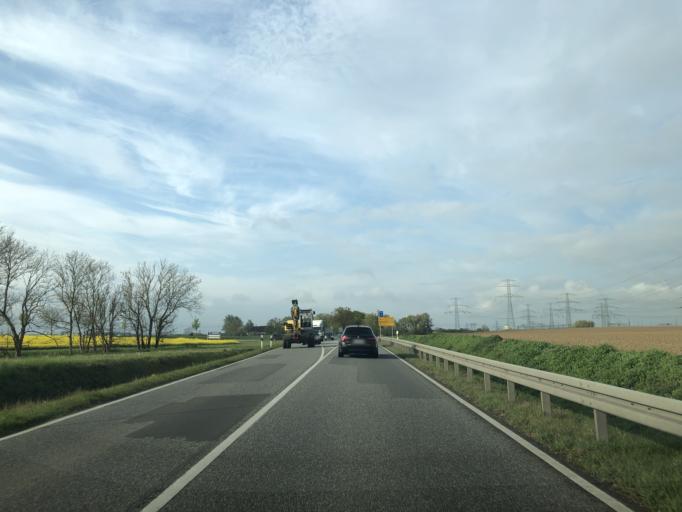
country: DE
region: Mecklenburg-Vorpommern
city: Guestrow
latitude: 53.8229
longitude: 12.2008
